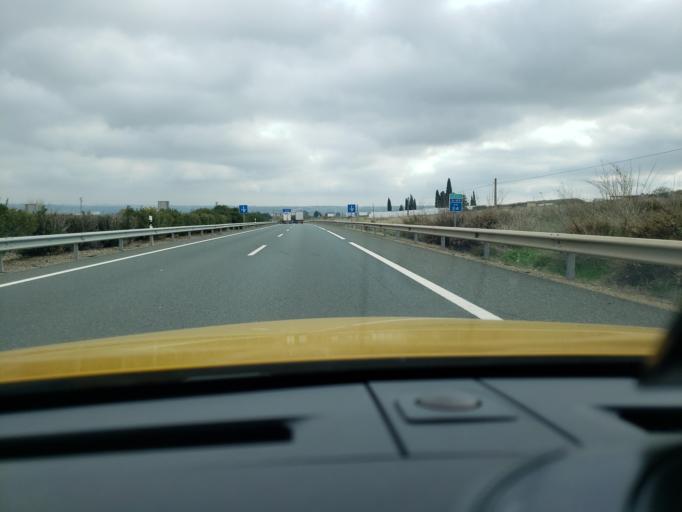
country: ES
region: Andalusia
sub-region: Provincia de Sevilla
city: Carrion de los Cespedes
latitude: 37.3608
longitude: -6.2804
